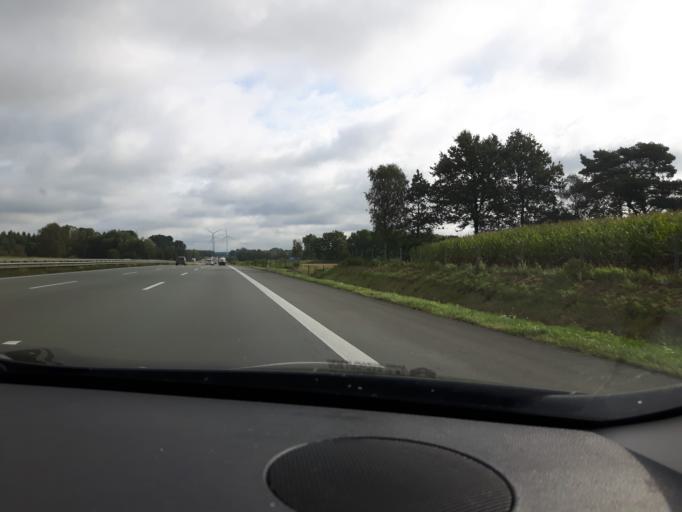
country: DE
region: Lower Saxony
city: Kalbe
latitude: 53.3143
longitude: 9.5679
